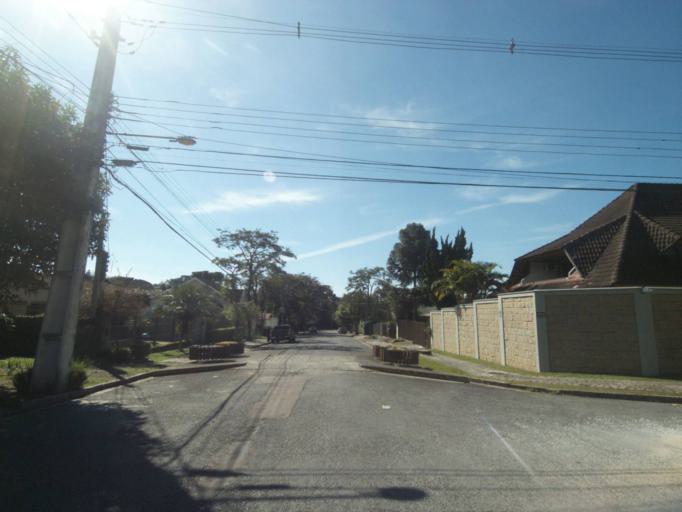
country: BR
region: Parana
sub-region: Curitiba
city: Curitiba
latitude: -25.4171
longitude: -49.2338
